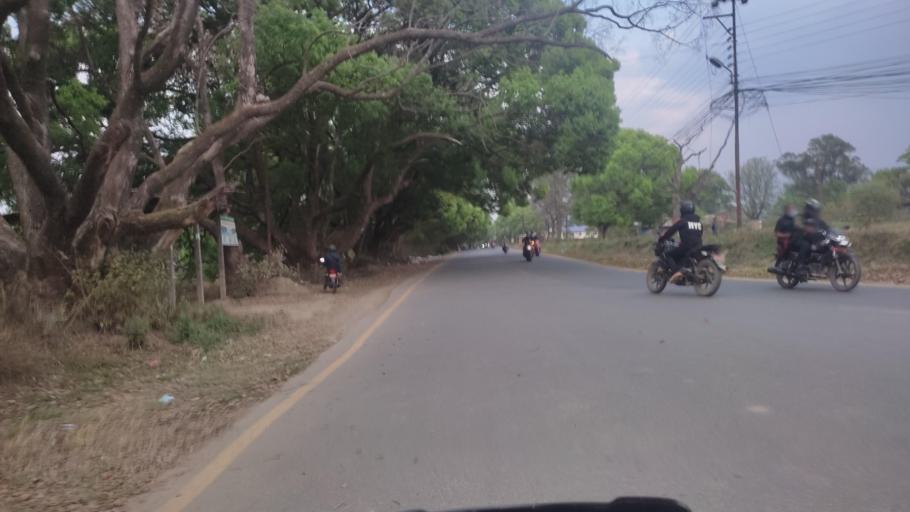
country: NP
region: Central Region
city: Kirtipur
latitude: 27.6786
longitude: 85.2851
